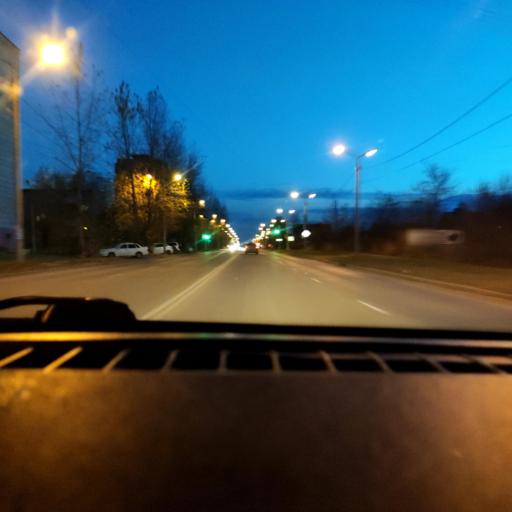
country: RU
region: Perm
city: Perm
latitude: 58.0588
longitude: 56.3590
